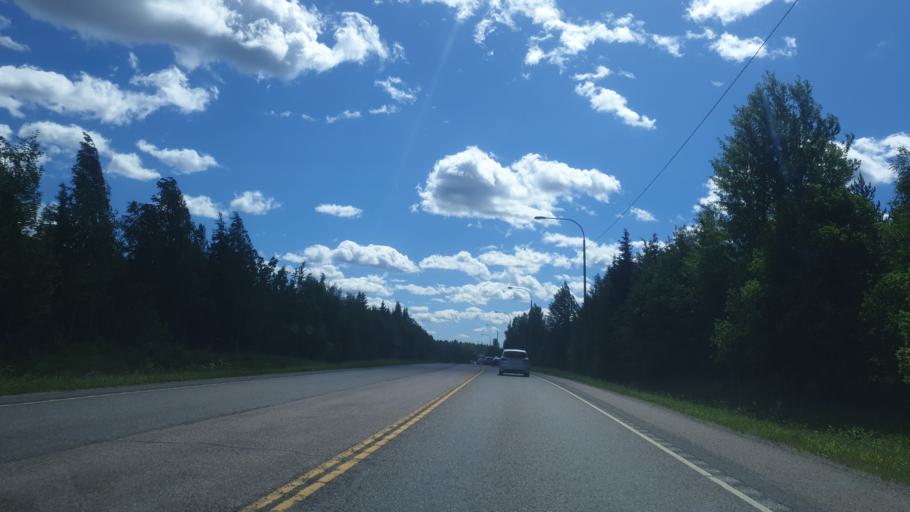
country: FI
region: Northern Savo
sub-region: Varkaus
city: Varkaus
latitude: 62.3595
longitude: 27.8111
